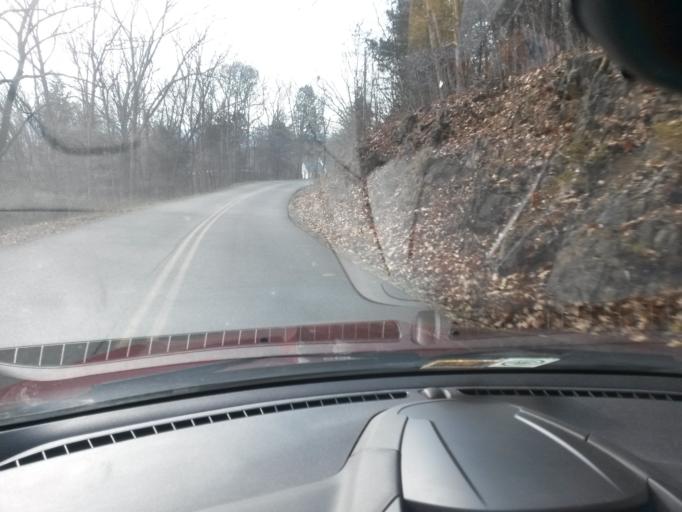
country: US
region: Virginia
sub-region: Botetourt County
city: Fincastle
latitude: 37.5543
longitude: -79.8758
